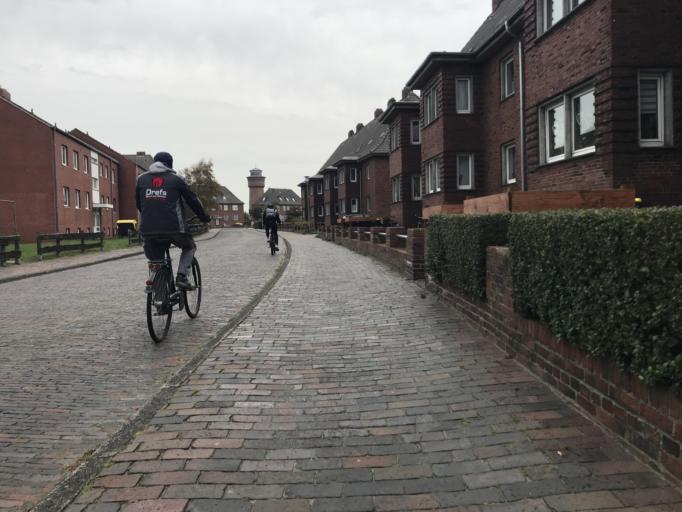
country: DE
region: Lower Saxony
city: Borkum
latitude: 53.5914
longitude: 6.6740
